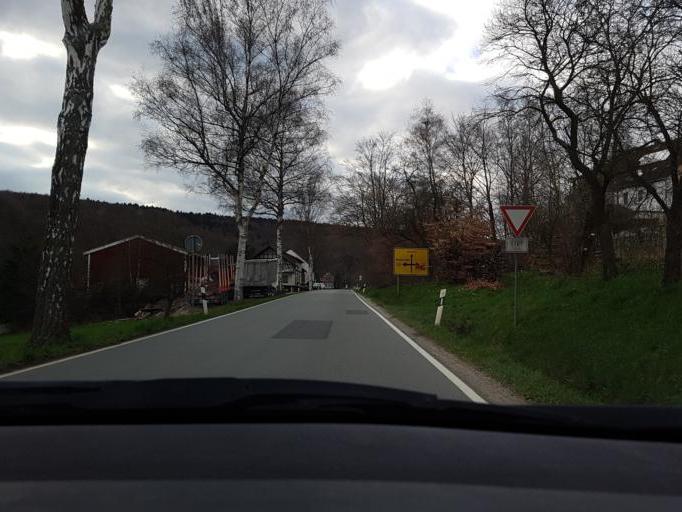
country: DE
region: Lower Saxony
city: Bodenfelde
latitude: 51.6897
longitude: 9.5209
